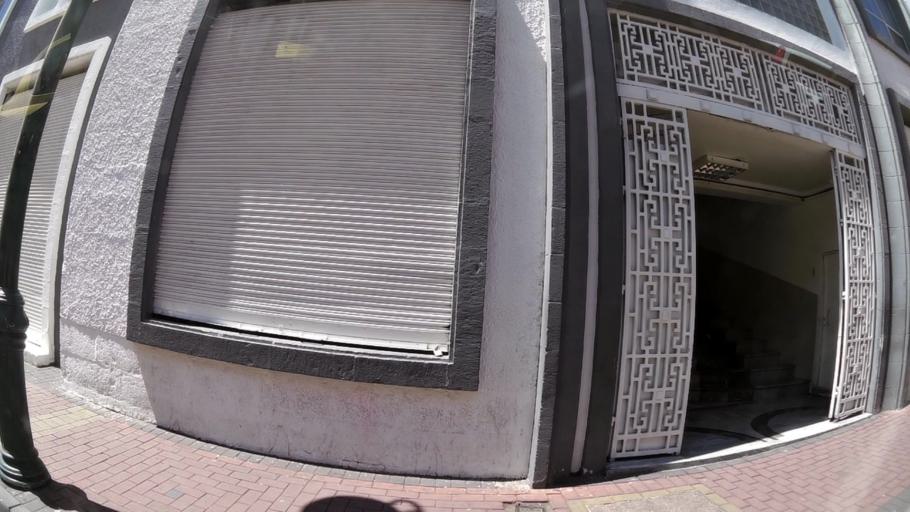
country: EC
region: Chimborazo
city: Riobamba
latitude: -1.6734
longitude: -78.6481
